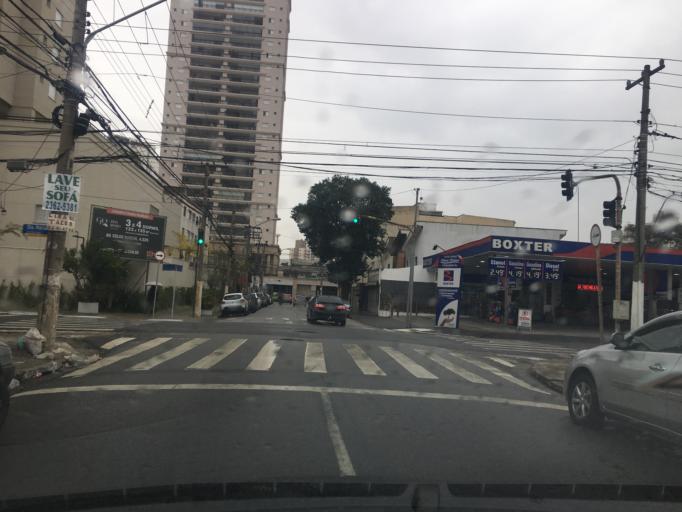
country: BR
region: Sao Paulo
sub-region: Sao Paulo
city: Sao Paulo
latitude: -23.5325
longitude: -46.5689
